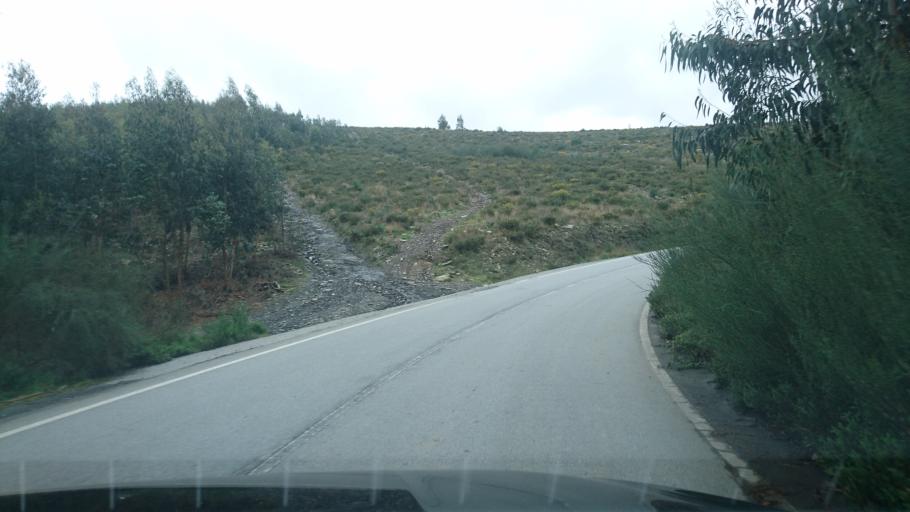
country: PT
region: Porto
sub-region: Paredes
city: Recarei
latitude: 41.1309
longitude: -8.3992
